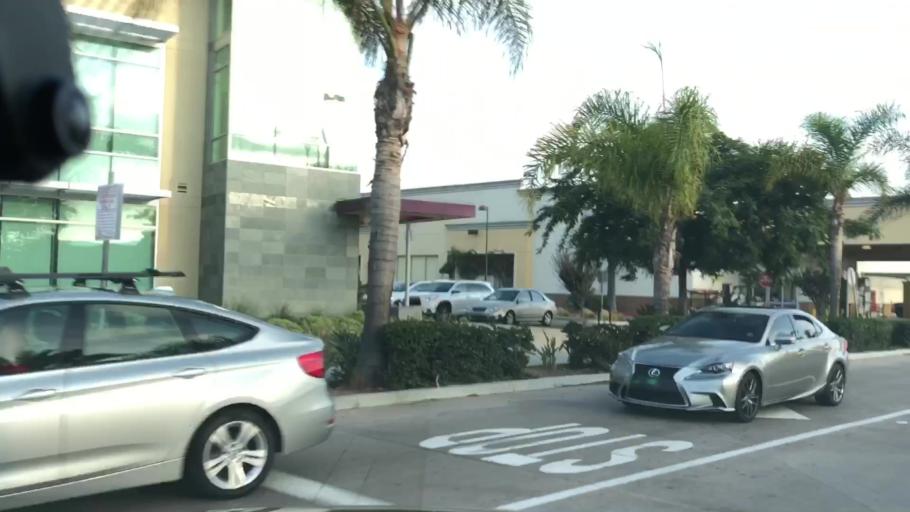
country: US
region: California
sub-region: Ventura County
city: Ventura
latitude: 34.2674
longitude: -119.2453
